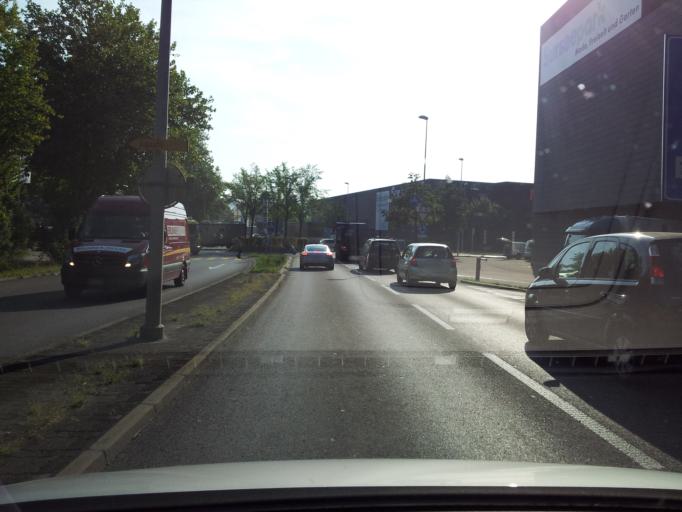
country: CH
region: Lucerne
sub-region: Sursee District
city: Sursee
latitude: 47.1732
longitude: 8.1000
